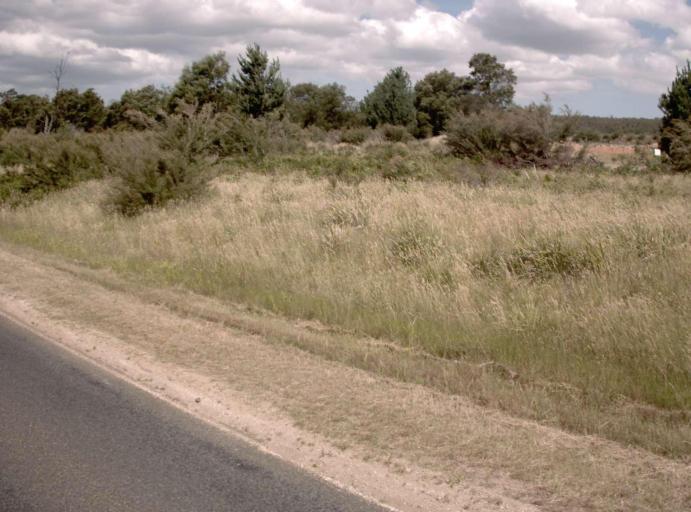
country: AU
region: Victoria
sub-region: Wellington
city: Sale
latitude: -38.1620
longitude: 146.8772
